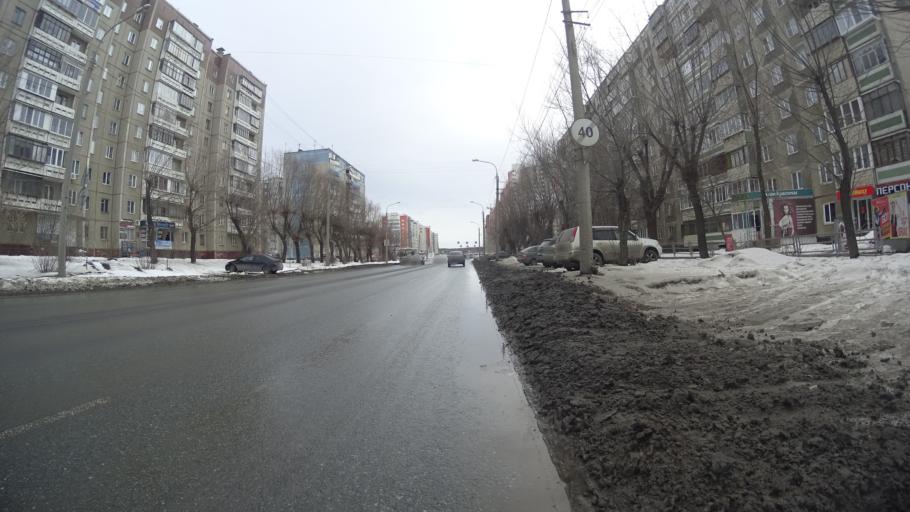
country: RU
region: Chelyabinsk
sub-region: Gorod Chelyabinsk
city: Chelyabinsk
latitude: 55.1781
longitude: 61.3096
